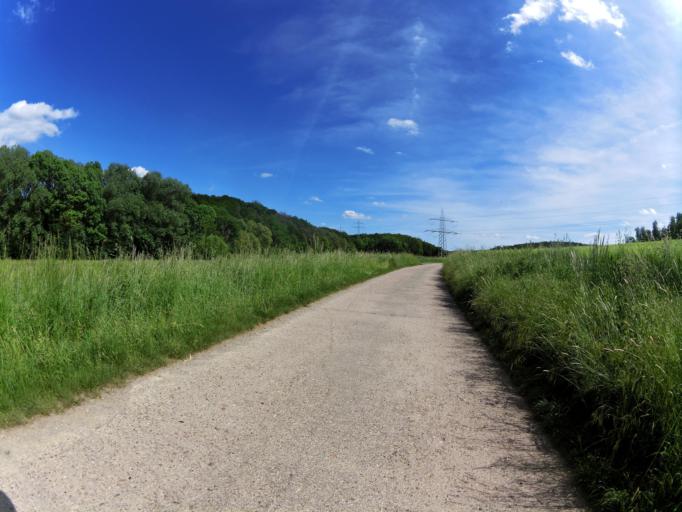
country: DE
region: Bavaria
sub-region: Regierungsbezirk Unterfranken
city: Uettingen
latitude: 49.7891
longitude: 9.7436
